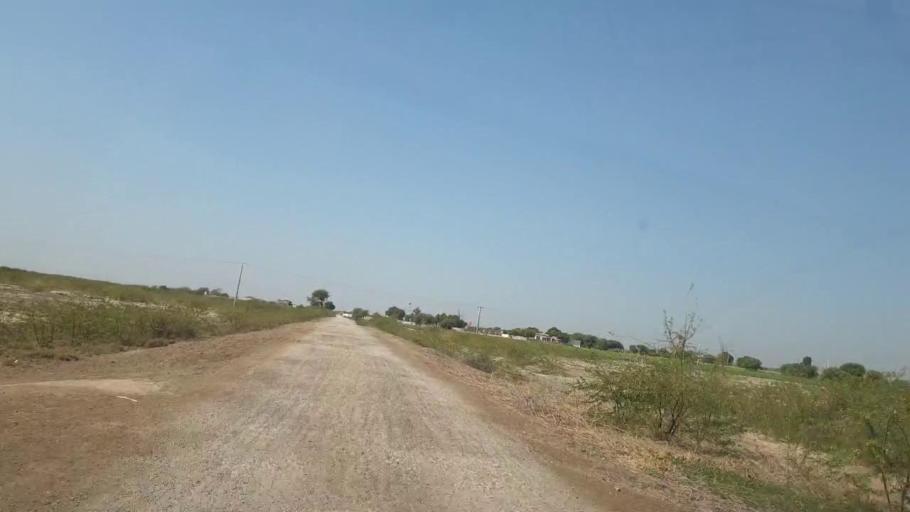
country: PK
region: Sindh
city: Kunri
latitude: 25.1137
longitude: 69.5257
